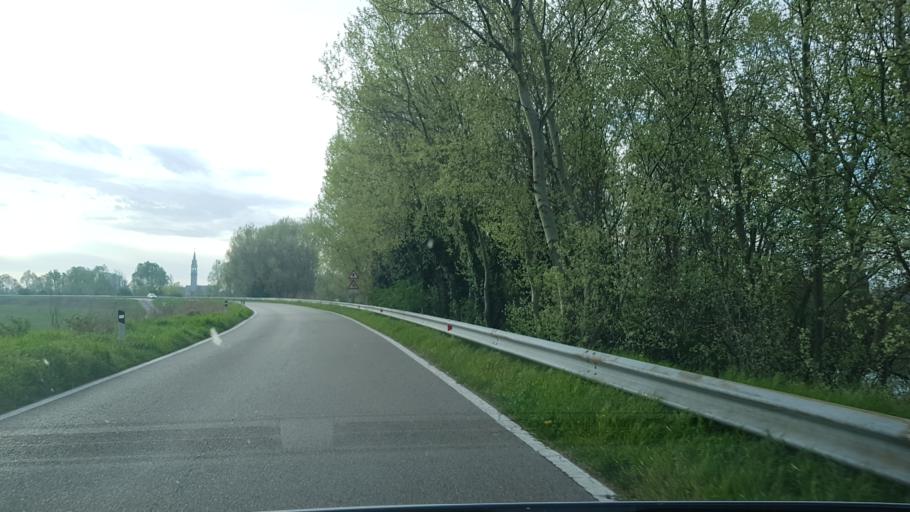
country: IT
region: Veneto
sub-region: Provincia di Padova
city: Barbona
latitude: 45.0994
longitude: 11.7205
